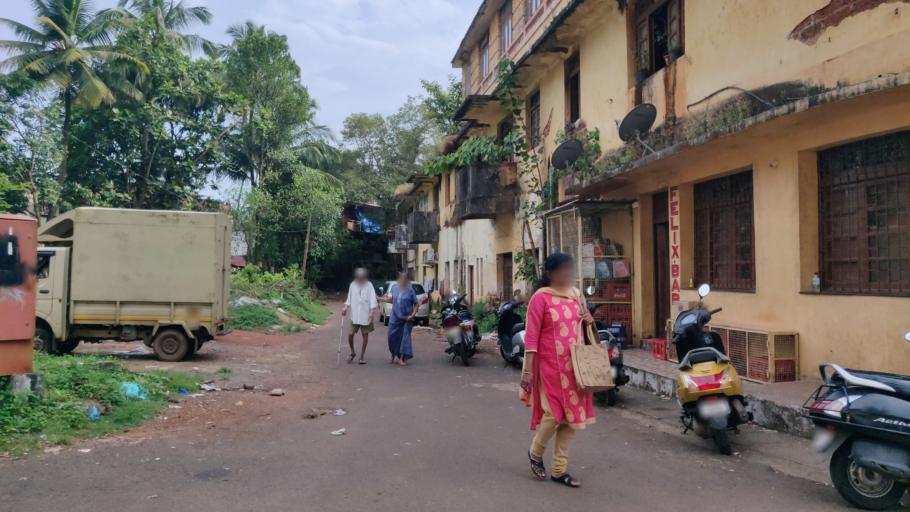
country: IN
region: Goa
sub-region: North Goa
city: Panaji
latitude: 15.4936
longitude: 73.8304
